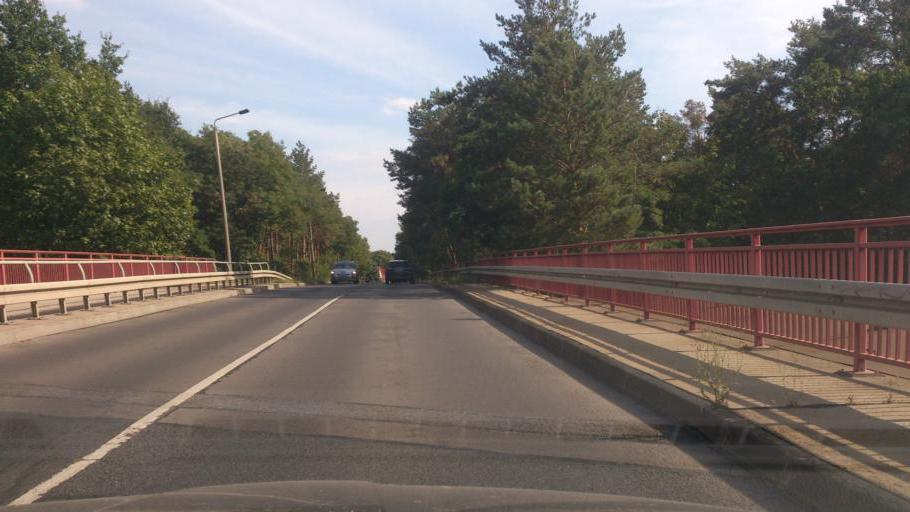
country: DE
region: Brandenburg
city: Ludwigsfelde
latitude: 52.3175
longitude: 13.2331
